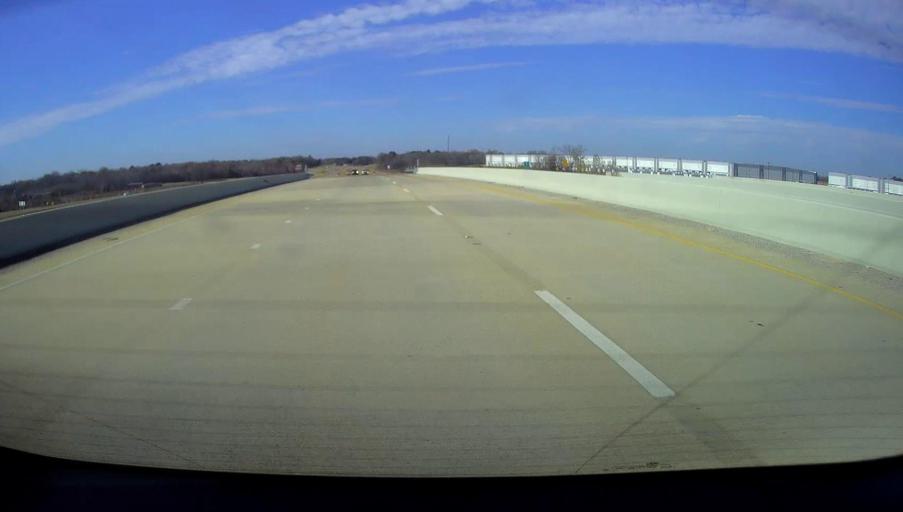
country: US
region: Tennessee
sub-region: Fayette County
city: Piperton
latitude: 34.9857
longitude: -89.5964
